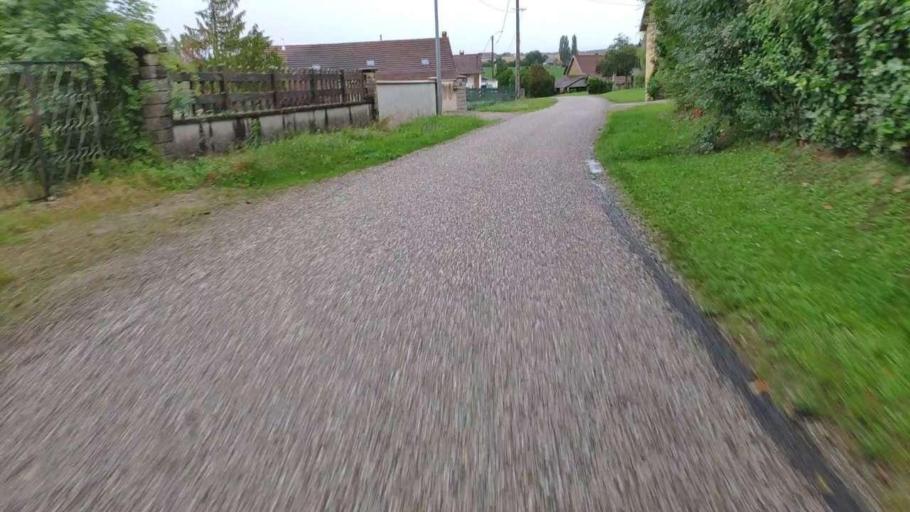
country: FR
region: Franche-Comte
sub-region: Departement du Jura
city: Chaussin
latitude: 46.8757
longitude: 5.4148
